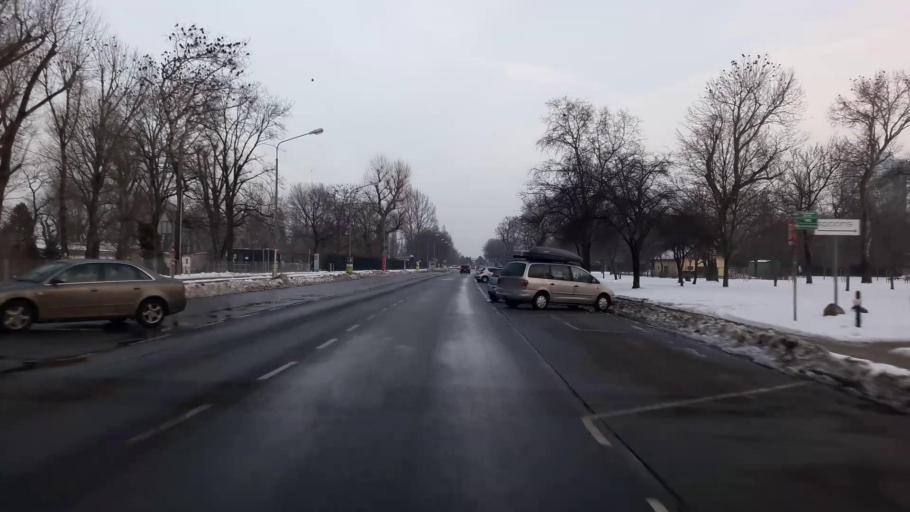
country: AT
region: Vienna
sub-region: Wien Stadt
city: Vienna
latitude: 48.2430
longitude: 16.4146
